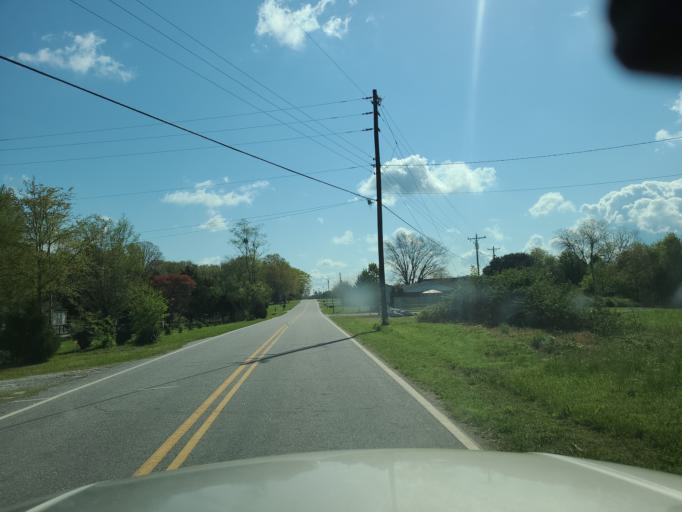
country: US
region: North Carolina
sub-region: Rutherford County
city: Spindale
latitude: 35.2966
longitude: -81.9212
